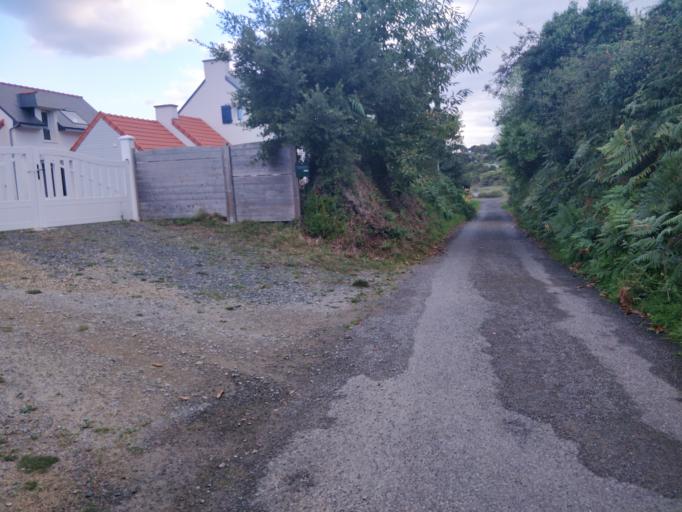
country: FR
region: Brittany
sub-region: Departement des Cotes-d'Armor
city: Tregastel
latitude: 48.8229
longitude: -3.4927
